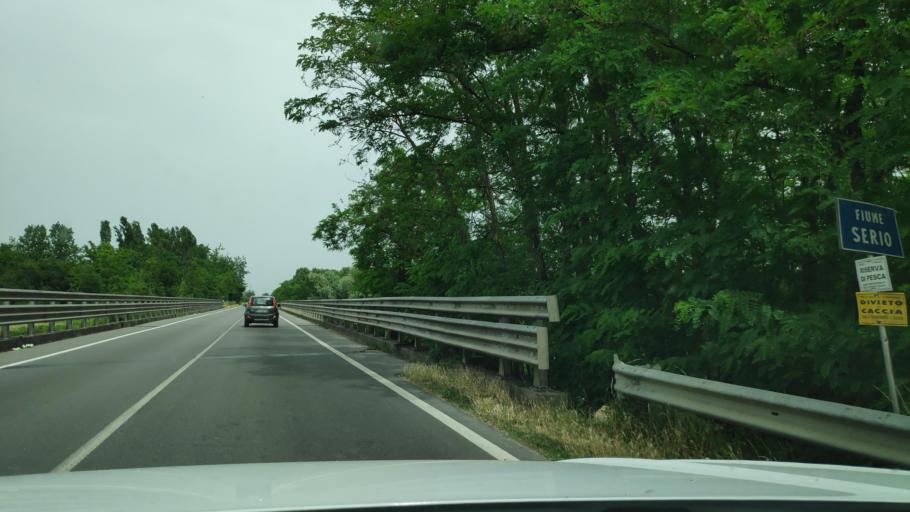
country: IT
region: Lombardy
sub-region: Provincia di Cremona
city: Ricengo
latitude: 45.4121
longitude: 9.7107
